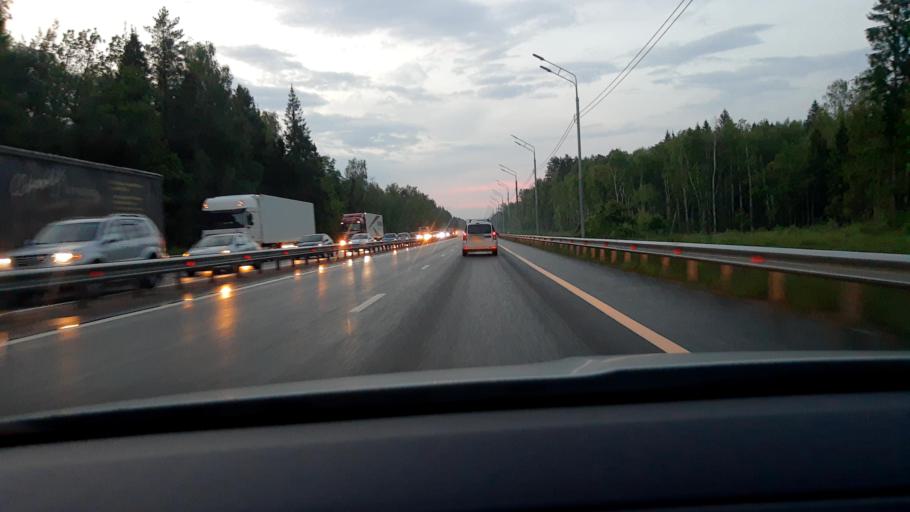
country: RU
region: Moskovskaya
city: Yershovo
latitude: 55.7685
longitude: 36.9041
